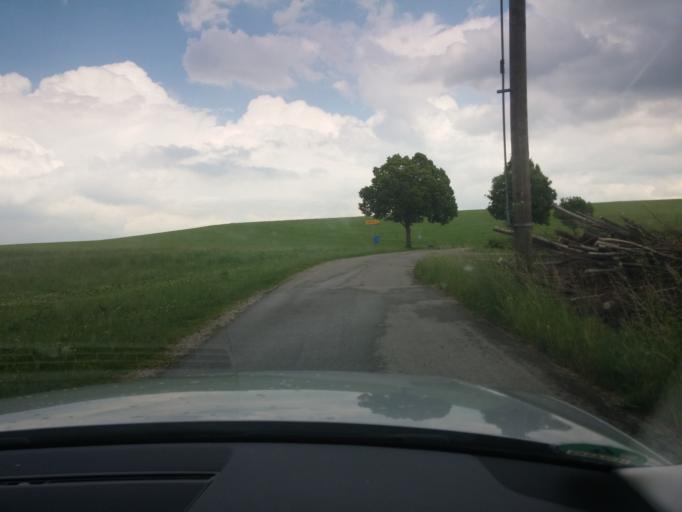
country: DE
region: Bavaria
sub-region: Swabia
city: Altusried
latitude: 47.8196
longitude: 10.1970
